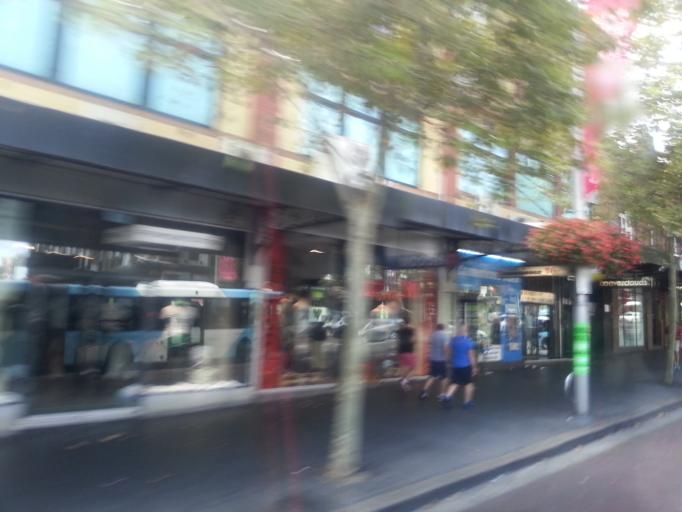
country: AU
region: New South Wales
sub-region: City of Sydney
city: Darlinghurst
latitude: -33.8778
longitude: 151.2138
